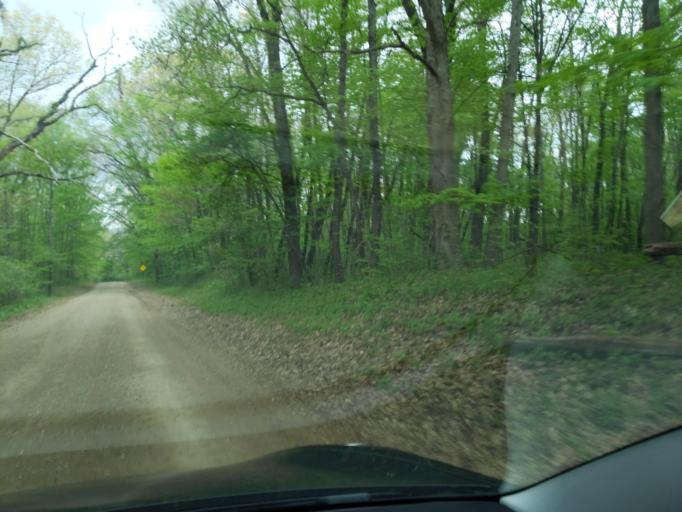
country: US
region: Michigan
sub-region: Ingham County
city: Stockbridge
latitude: 42.5250
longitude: -84.2967
